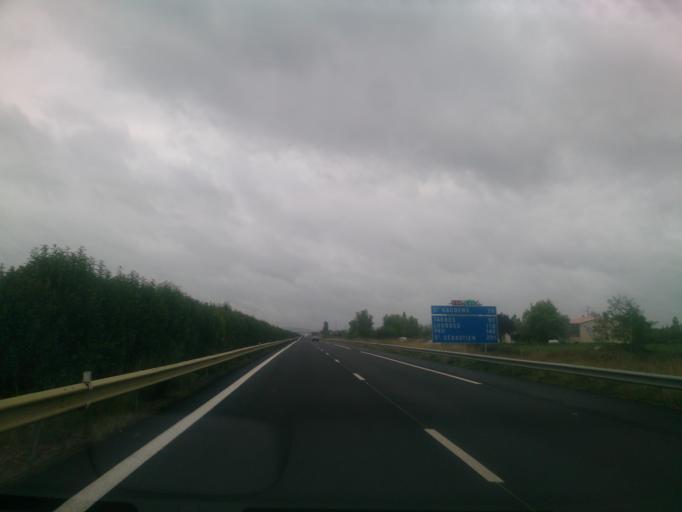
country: FR
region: Midi-Pyrenees
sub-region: Departement de la Haute-Garonne
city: Cazeres
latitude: 43.2327
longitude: 1.0677
